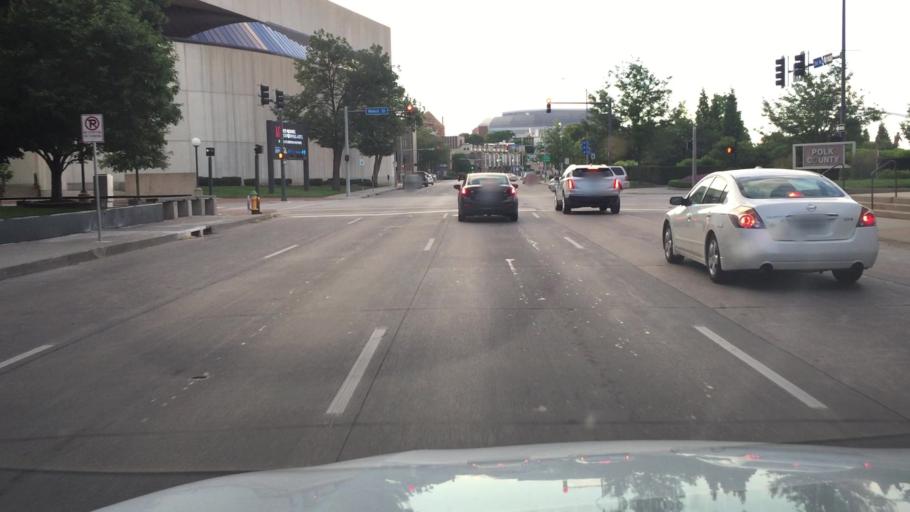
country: US
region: Iowa
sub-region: Polk County
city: Des Moines
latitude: 41.5866
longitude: -93.6196
